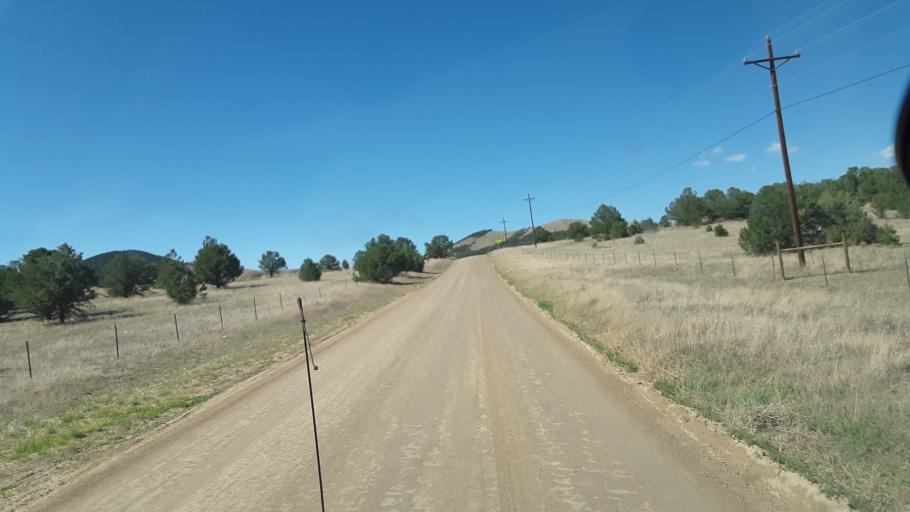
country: US
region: Colorado
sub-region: Custer County
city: Westcliffe
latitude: 38.3037
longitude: -105.4865
